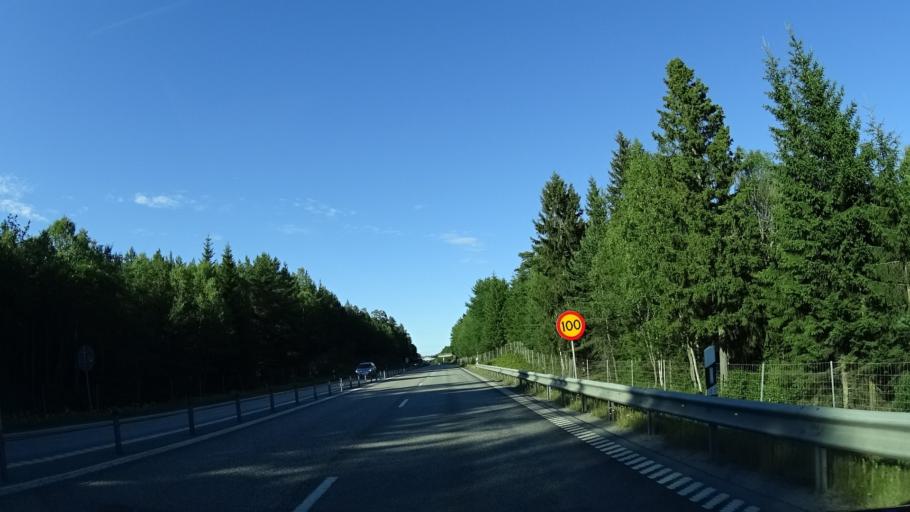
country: SE
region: Stockholm
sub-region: Osterakers Kommun
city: Akersberga
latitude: 59.5358
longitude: 18.2020
